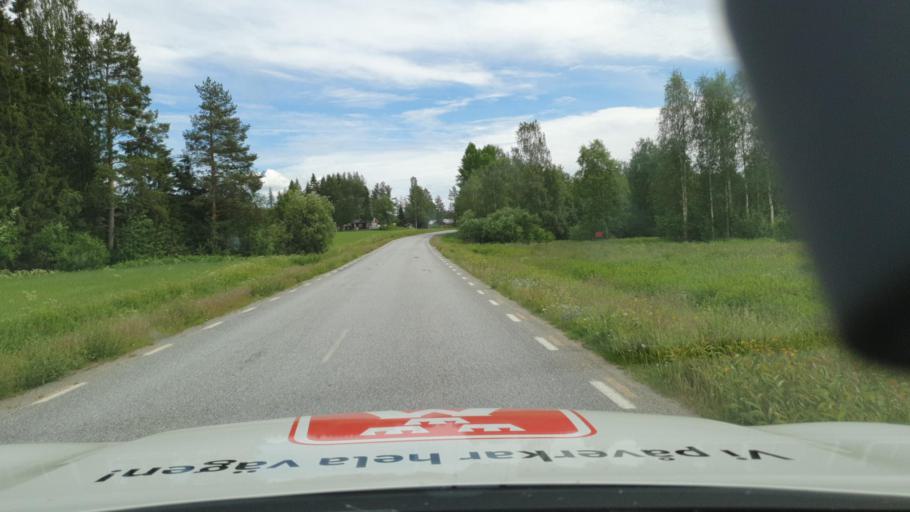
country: SE
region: Vaesterbotten
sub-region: Skelleftea Kommun
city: Soedra Bergsbyn
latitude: 64.5121
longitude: 20.9973
